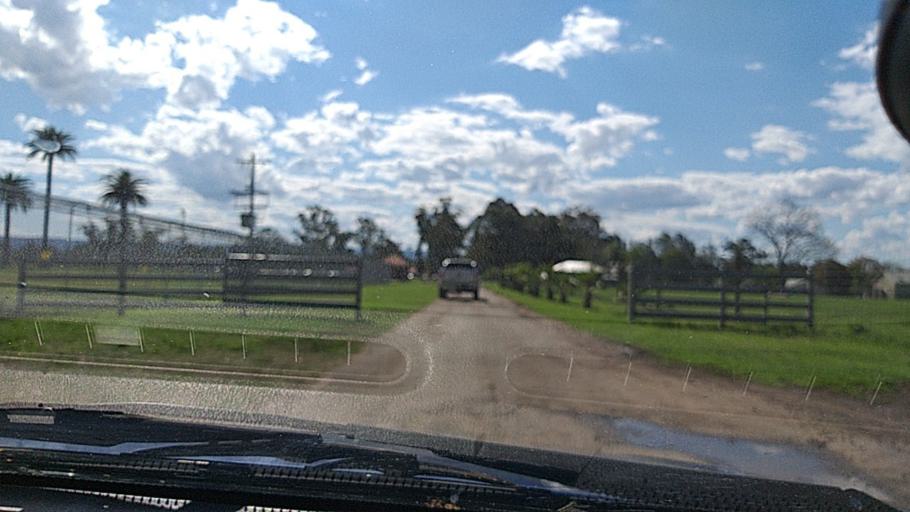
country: AU
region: New South Wales
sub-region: Hawkesbury
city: Richmond
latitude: -33.6176
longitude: 150.7559
